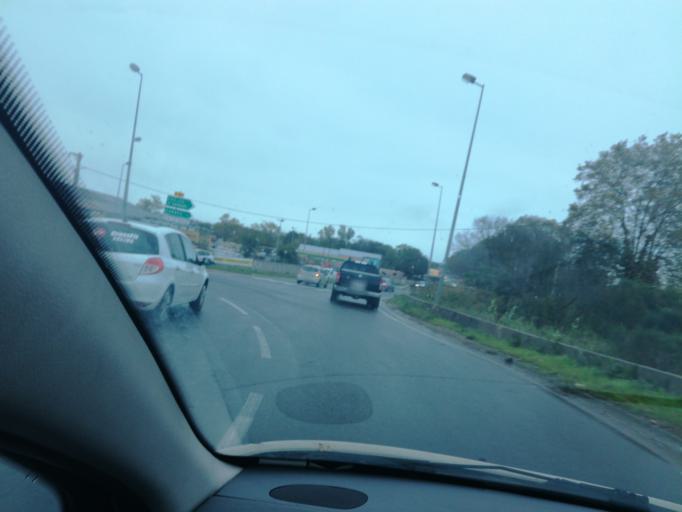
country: FR
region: Provence-Alpes-Cote d'Azur
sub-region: Departement du Var
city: Puget-sur-Argens
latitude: 43.4393
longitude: 6.7072
